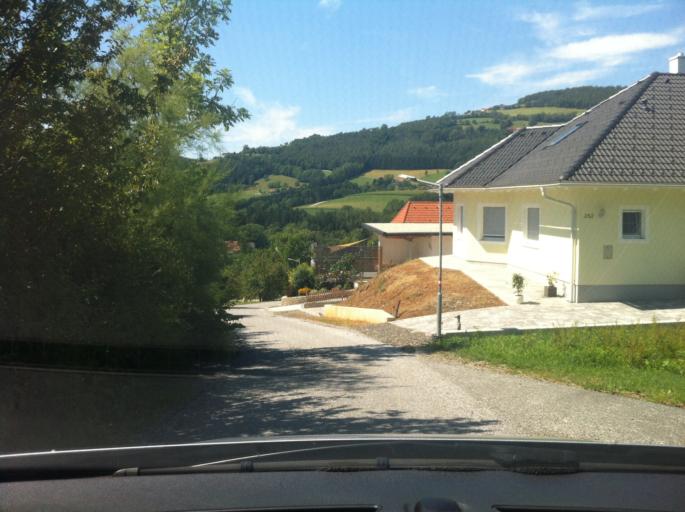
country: AT
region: Styria
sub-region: Politischer Bezirk Hartberg-Fuerstenfeld
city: Stubenberg
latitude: 47.2431
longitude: 15.8002
